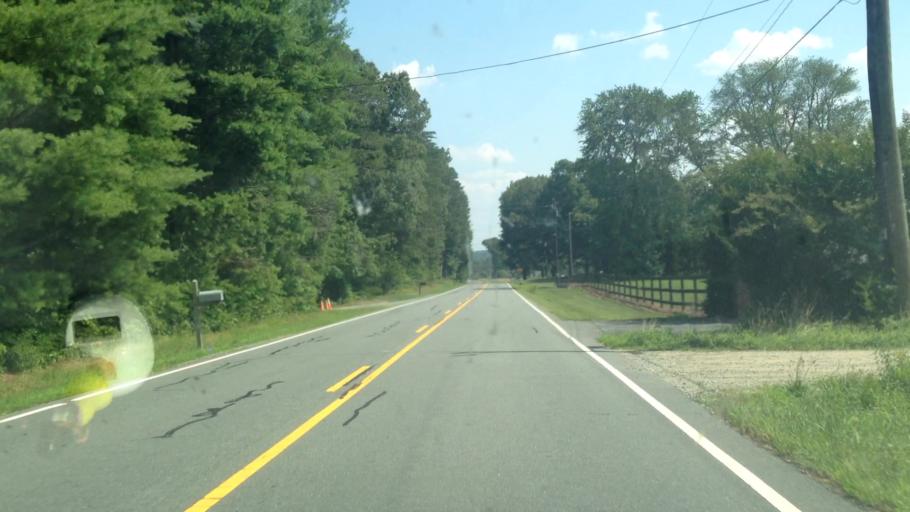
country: US
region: North Carolina
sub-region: Stokes County
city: Walnut Cove
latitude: 36.3446
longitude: -80.0529
